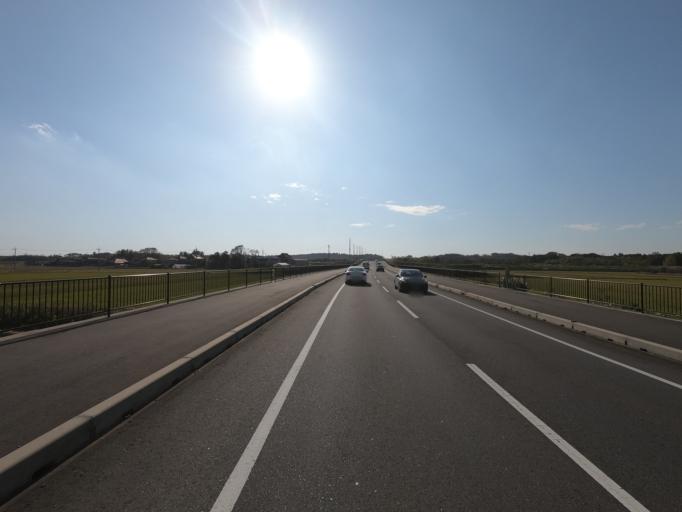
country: JP
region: Ibaraki
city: Naka
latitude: 36.1233
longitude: 140.1351
